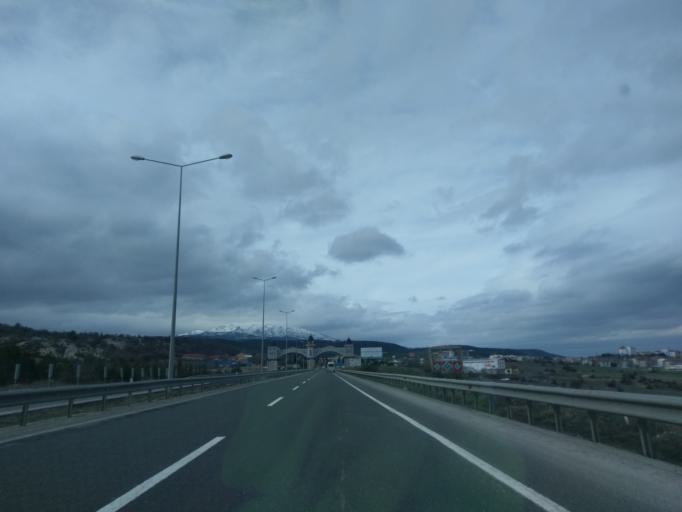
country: TR
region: Kuetahya
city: Kutahya
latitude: 39.3759
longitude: 30.0595
